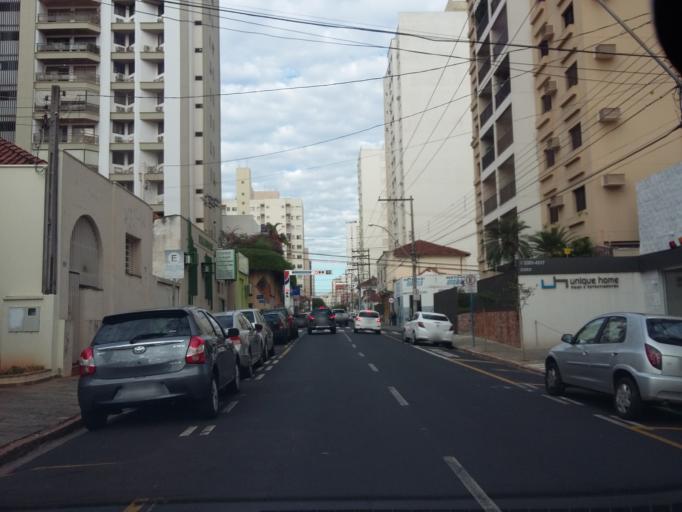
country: BR
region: Sao Paulo
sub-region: Sao Jose Do Rio Preto
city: Sao Jose do Rio Preto
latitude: -20.8117
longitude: -49.3852
